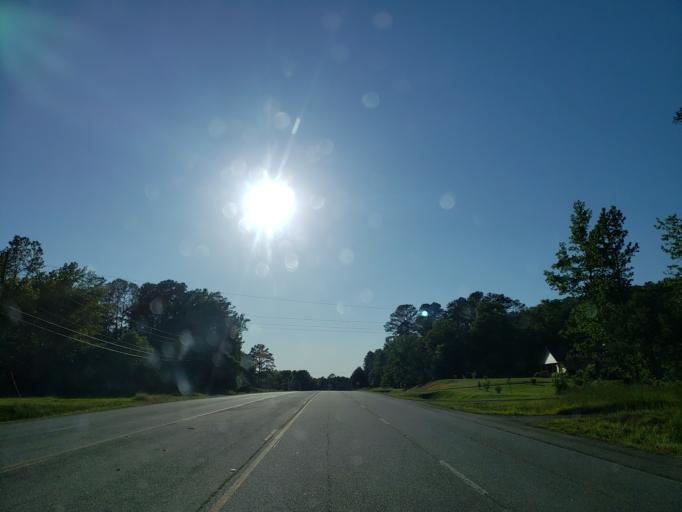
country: US
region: Georgia
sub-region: Polk County
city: Cedartown
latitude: 33.9575
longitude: -85.2527
